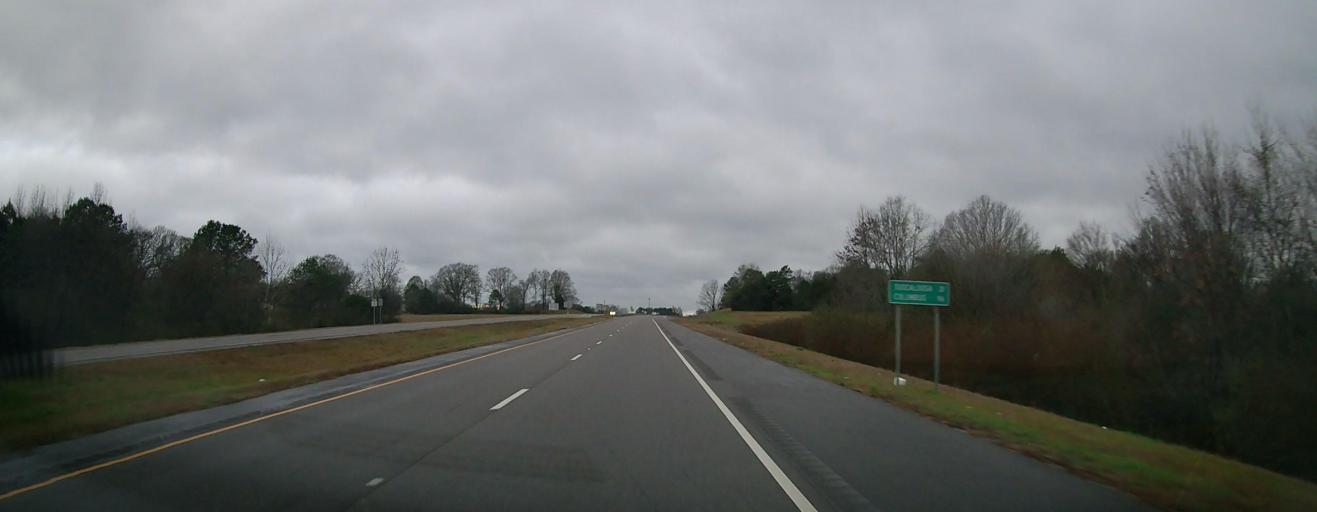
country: US
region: Alabama
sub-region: Bibb County
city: Centreville
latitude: 32.9581
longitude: -87.1413
